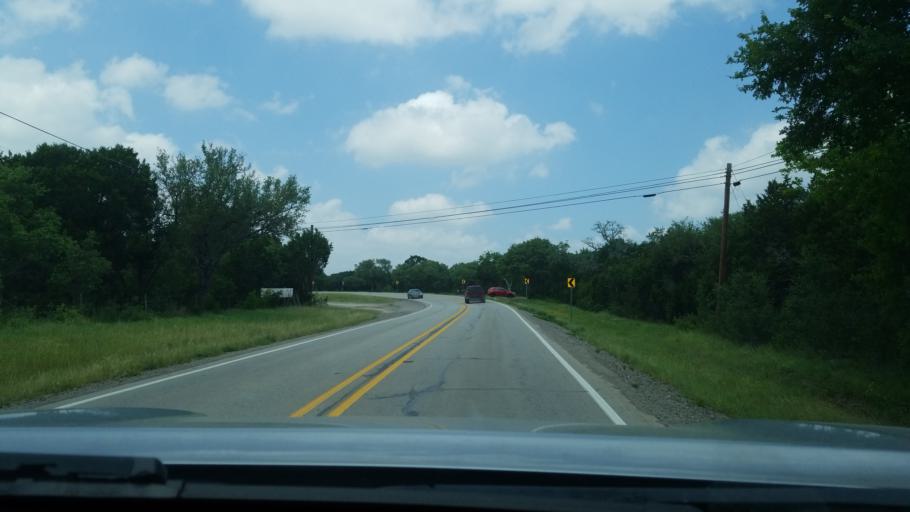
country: US
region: Texas
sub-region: Hays County
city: Dripping Springs
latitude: 30.1573
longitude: -98.0674
